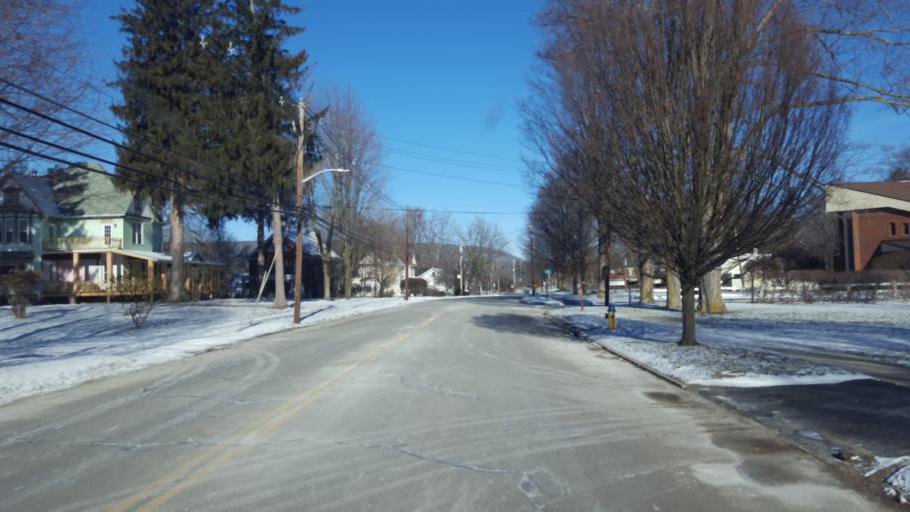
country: US
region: New York
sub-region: Allegany County
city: Wellsville
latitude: 42.1274
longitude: -77.9571
